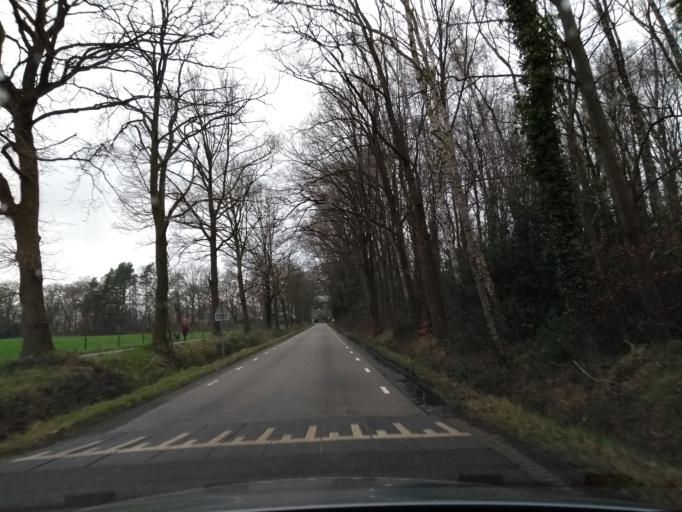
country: NL
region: Overijssel
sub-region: Gemeente Enschede
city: Enschede
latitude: 52.2115
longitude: 6.9302
